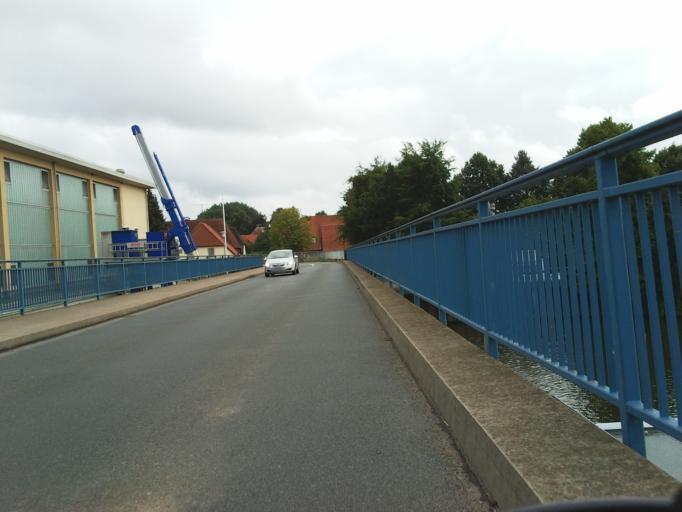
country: DE
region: Lower Saxony
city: Drakenburg
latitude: 52.6886
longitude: 9.2103
